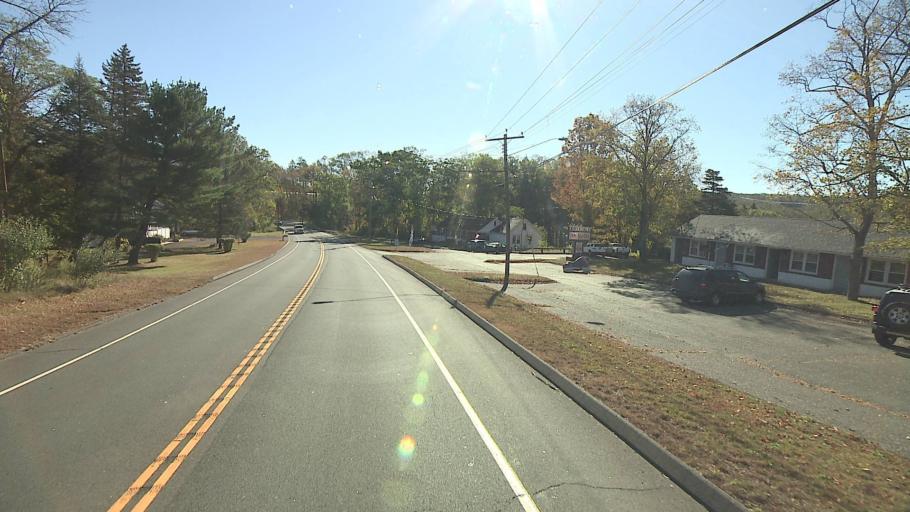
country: US
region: Connecticut
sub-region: Middlesex County
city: Portland
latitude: 41.5620
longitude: -72.5852
